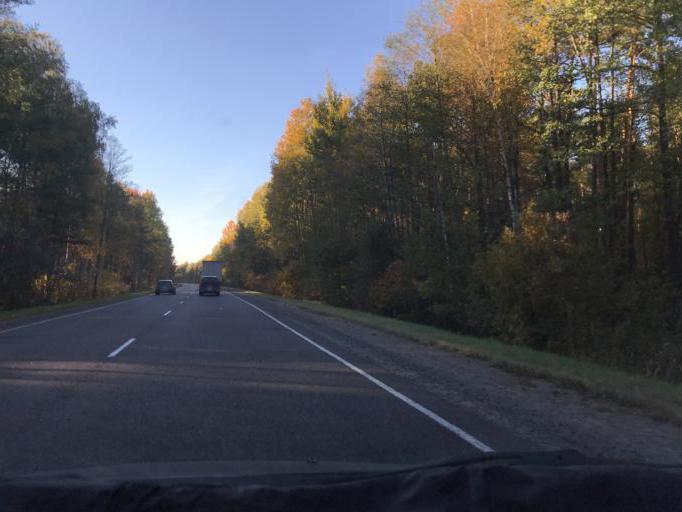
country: BY
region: Gomel
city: Pyetrykaw
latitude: 52.2550
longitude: 28.3520
